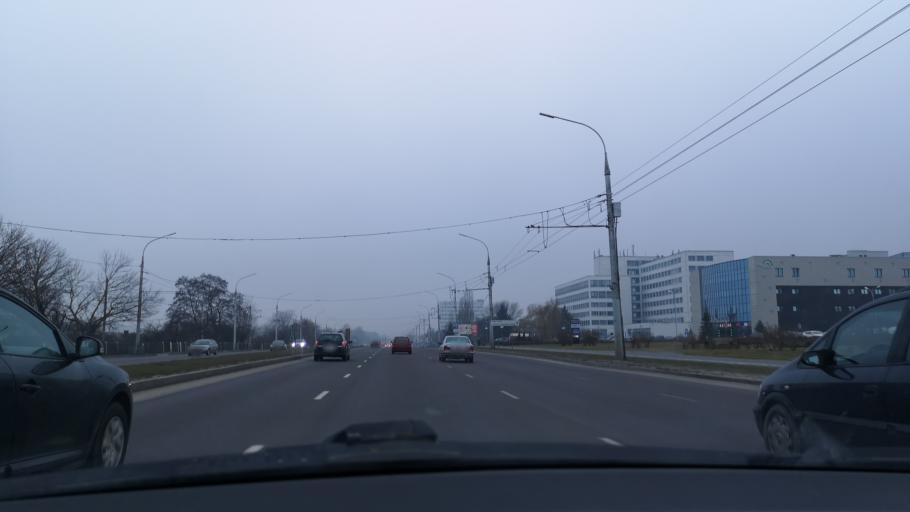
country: BY
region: Brest
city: Brest
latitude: 52.0959
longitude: 23.7437
